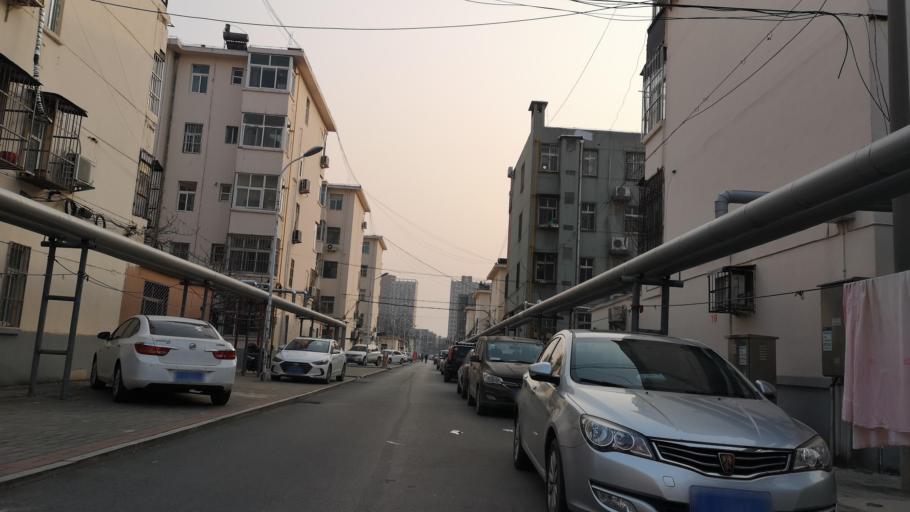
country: CN
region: Henan Sheng
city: Zhongyuanlu
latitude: 35.7681
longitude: 115.1018
